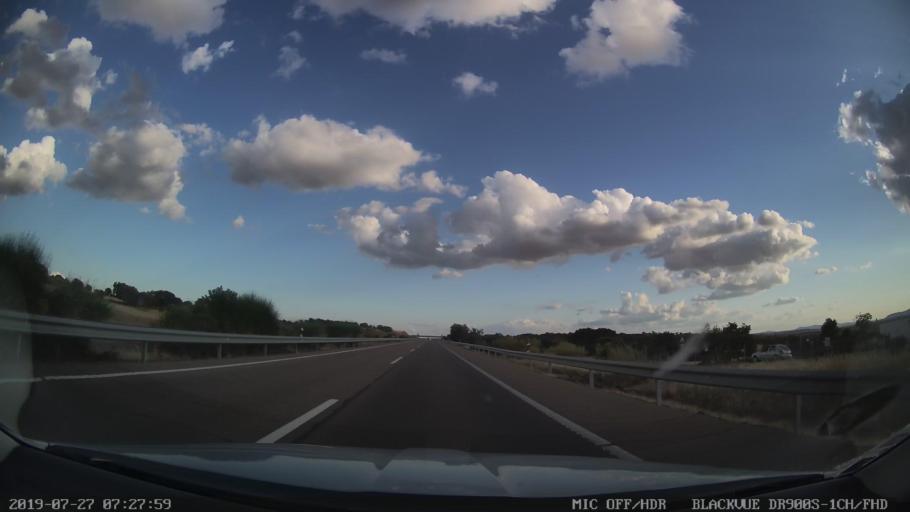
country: ES
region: Extremadura
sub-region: Provincia de Caceres
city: Villamesias
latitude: 39.2353
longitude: -5.8832
